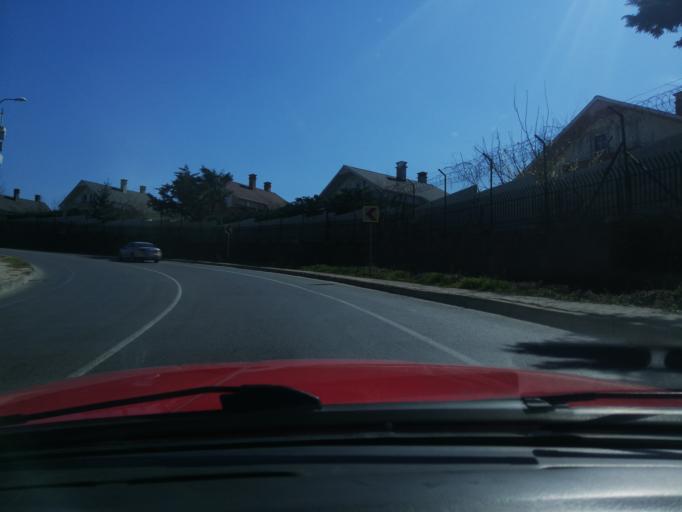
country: TR
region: Istanbul
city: Mahmut Sevket Pasa
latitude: 41.1220
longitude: 29.1327
